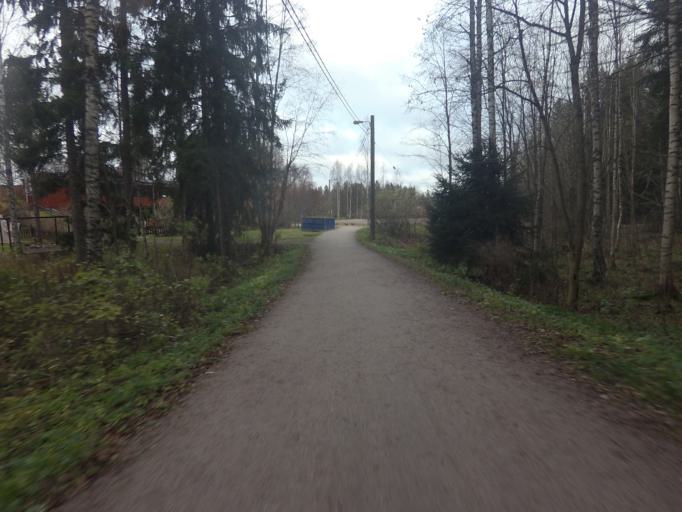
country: FI
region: Uusimaa
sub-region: Helsinki
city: Espoo
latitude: 60.1929
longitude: 24.6818
